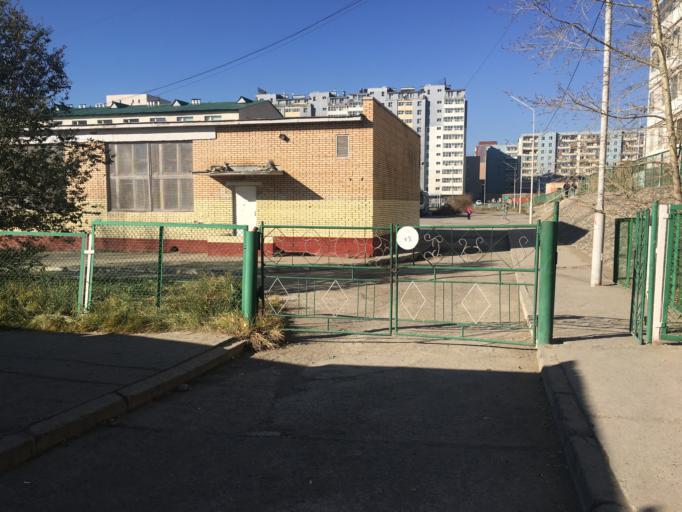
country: MN
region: Ulaanbaatar
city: Ulaanbaatar
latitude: 47.9211
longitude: 106.8864
